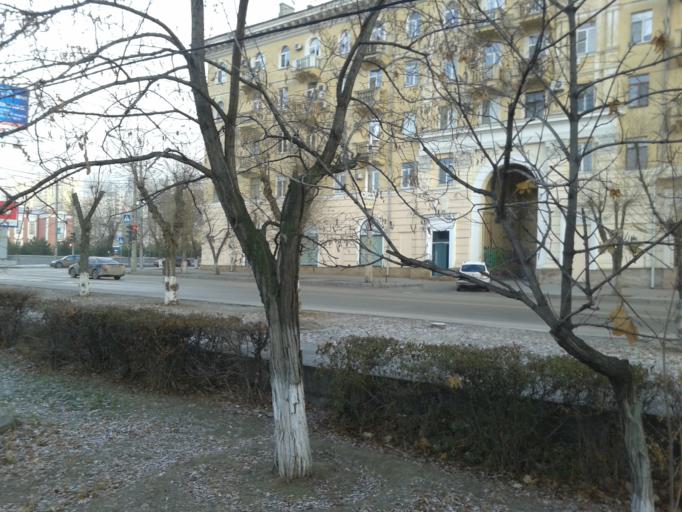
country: RU
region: Volgograd
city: Volgograd
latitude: 48.7093
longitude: 44.5113
